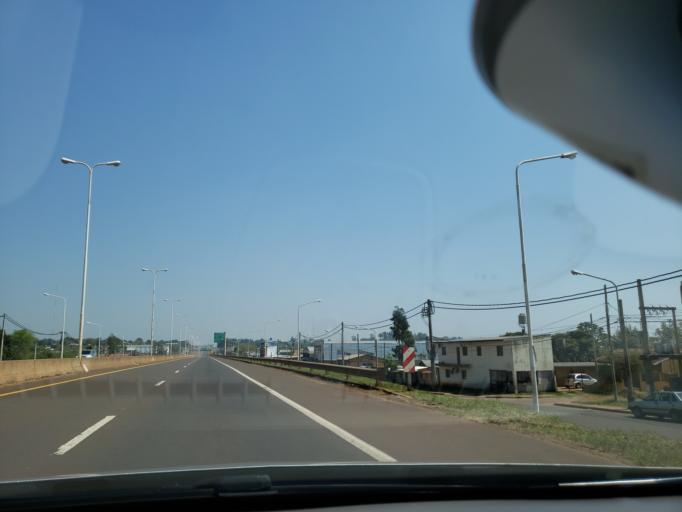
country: AR
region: Misiones
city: Garupa
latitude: -27.4606
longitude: -55.8469
